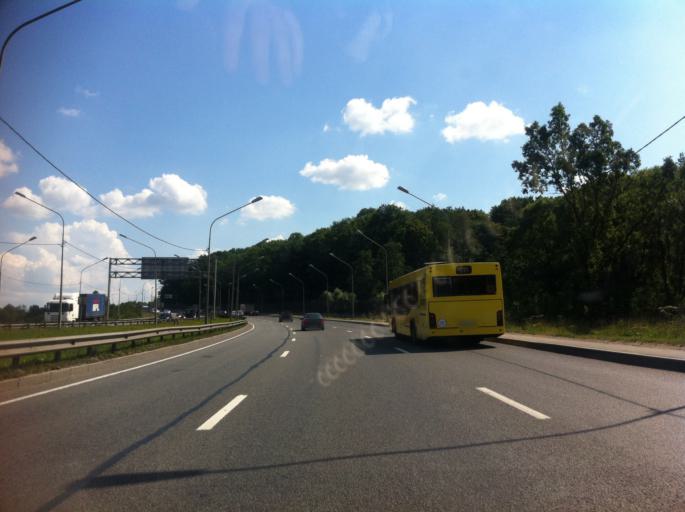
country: RU
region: St.-Petersburg
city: Aleksandrovskaya
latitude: 59.7767
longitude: 30.3256
